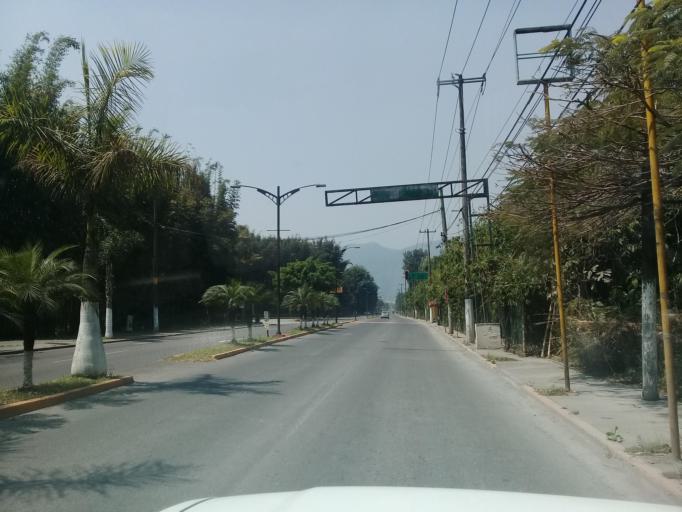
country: MX
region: Veracruz
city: Ixtac Zoquitlan
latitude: 18.8615
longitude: -97.0418
